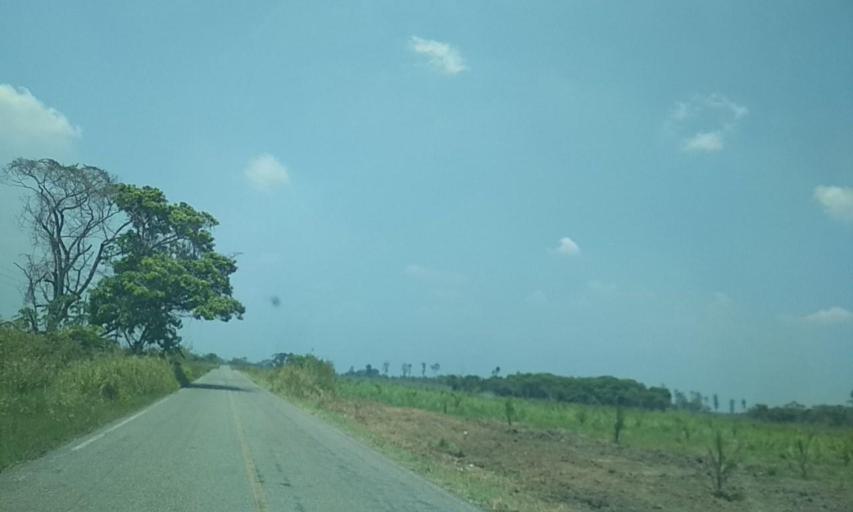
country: MX
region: Tabasco
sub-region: Huimanguillo
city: Paso de la Mina 3ra. Seccion
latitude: 17.8290
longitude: -93.6171
